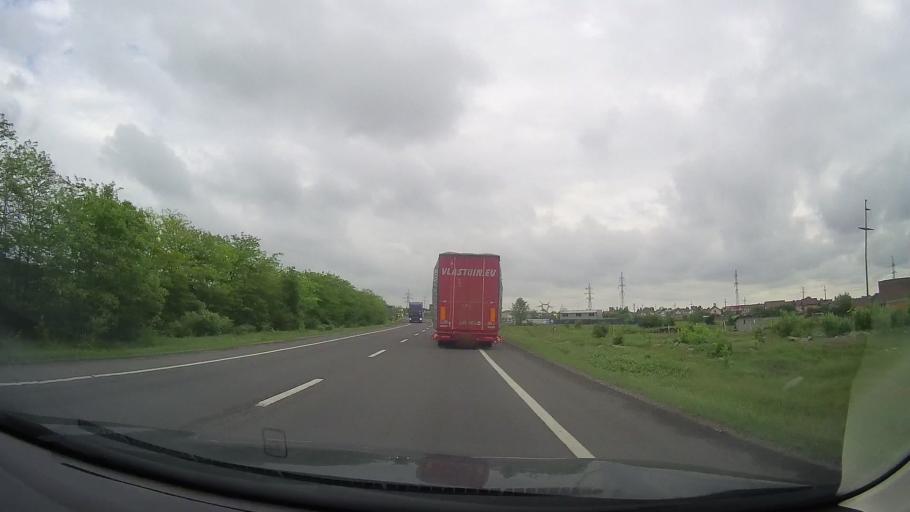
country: RO
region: Dolj
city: Craiova
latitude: 44.3465
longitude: 23.8293
